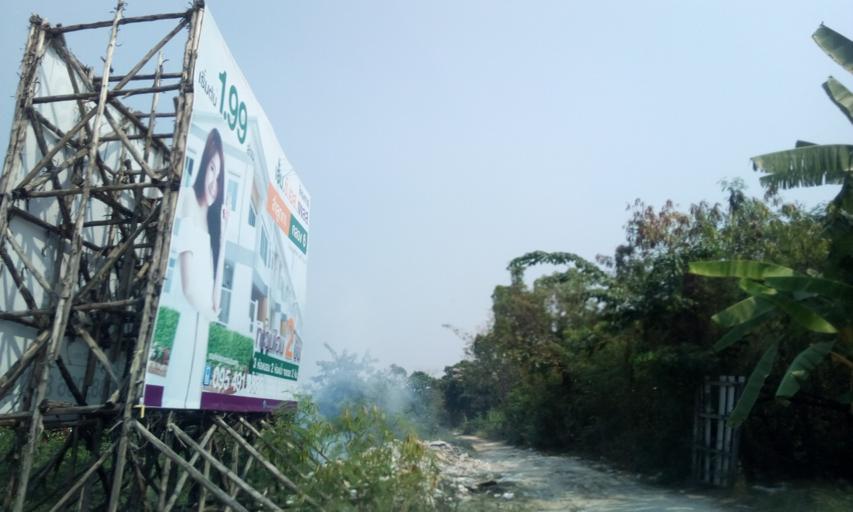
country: TH
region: Pathum Thani
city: Lam Luk Ka
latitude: 13.9553
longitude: 100.7251
